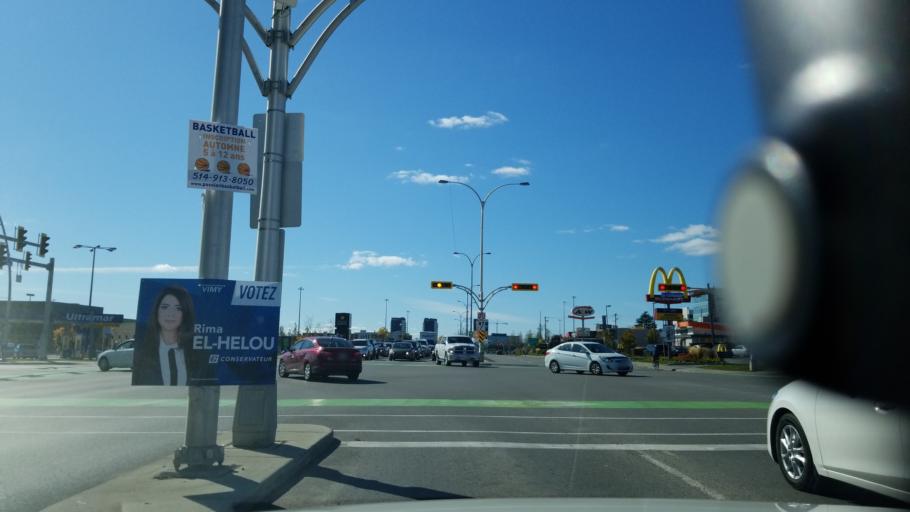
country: CA
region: Quebec
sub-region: Laval
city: Laval
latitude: 45.5655
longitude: -73.7322
